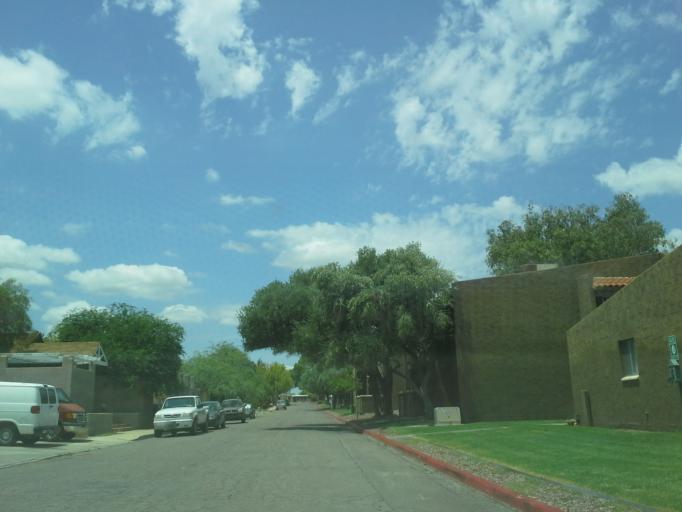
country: US
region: Arizona
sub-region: Pima County
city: Tucson
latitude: 32.2313
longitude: -110.9239
